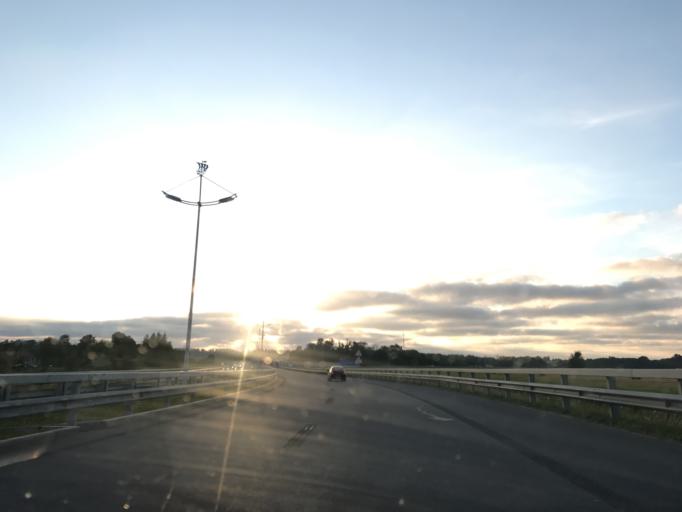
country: RU
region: Kaliningrad
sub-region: Gorod Kaliningrad
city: Pionerskiy
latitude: 54.9141
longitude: 20.1994
